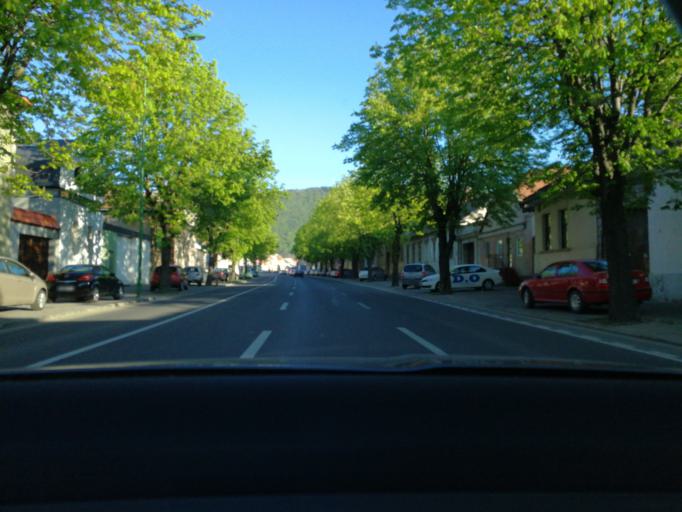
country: RO
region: Brasov
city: Brasov
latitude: 45.6535
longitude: 25.5841
